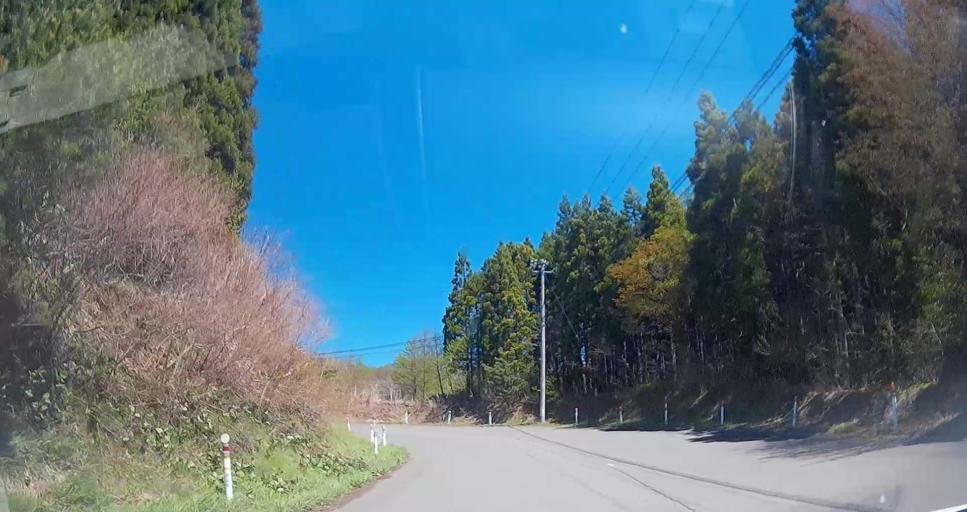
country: JP
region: Aomori
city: Mutsu
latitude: 41.2552
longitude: 141.3881
